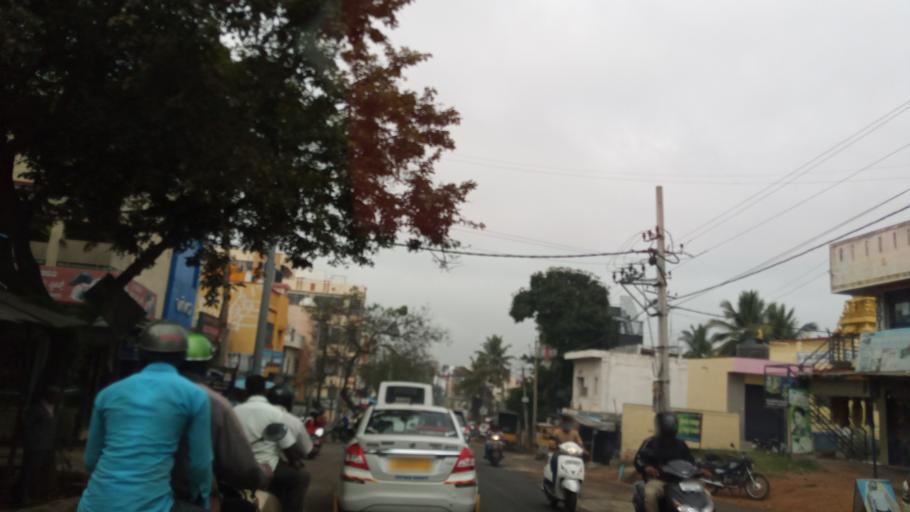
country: IN
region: Karnataka
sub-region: Bangalore Urban
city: Bangalore
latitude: 12.9032
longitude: 77.5169
